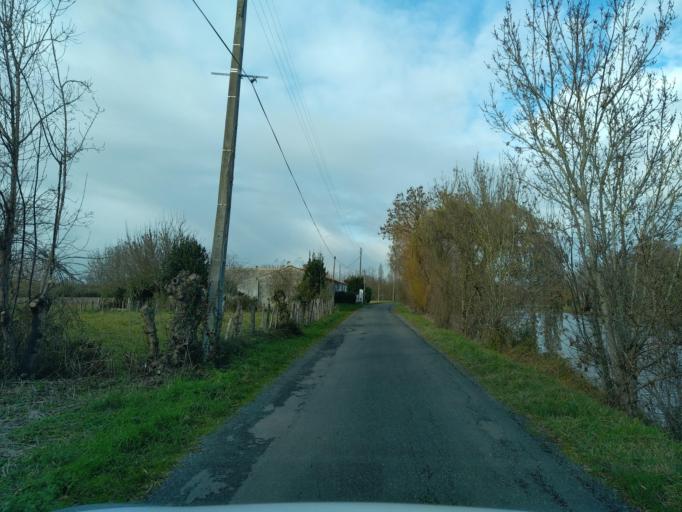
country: FR
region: Pays de la Loire
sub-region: Departement de la Vendee
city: Vix
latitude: 46.3297
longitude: -0.8071
